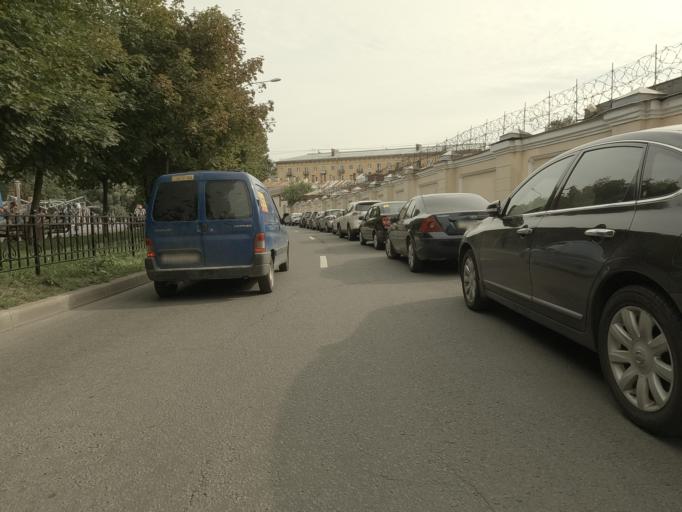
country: RU
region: St.-Petersburg
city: Admiralteisky
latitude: 59.9130
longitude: 30.2838
